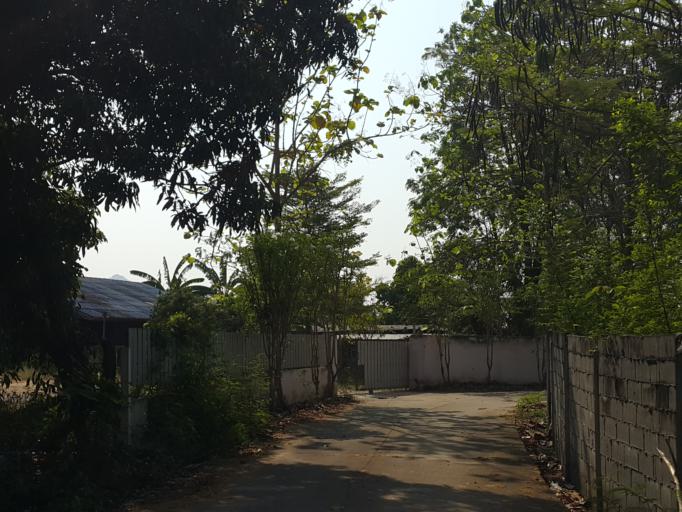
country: TH
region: Kanchanaburi
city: Sai Yok
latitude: 14.1131
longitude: 99.1367
